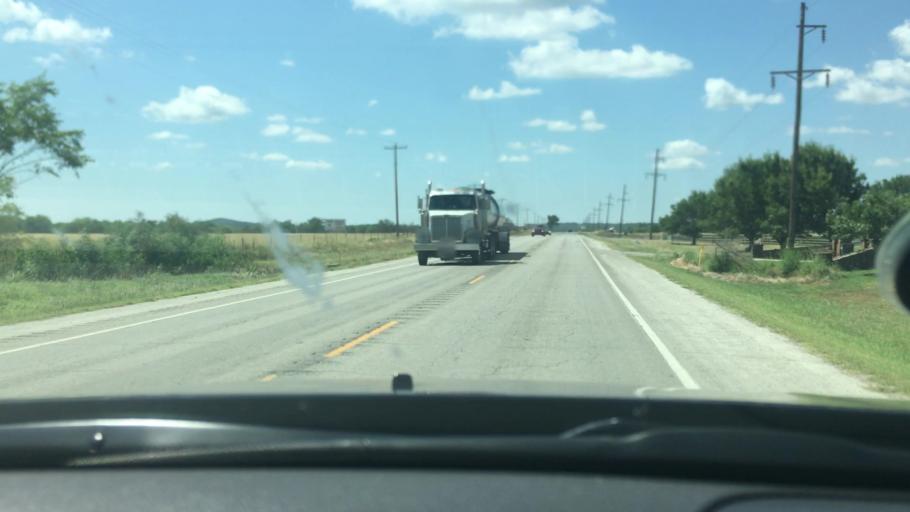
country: US
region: Oklahoma
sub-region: Carter County
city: Ardmore
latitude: 34.0922
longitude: -97.1429
